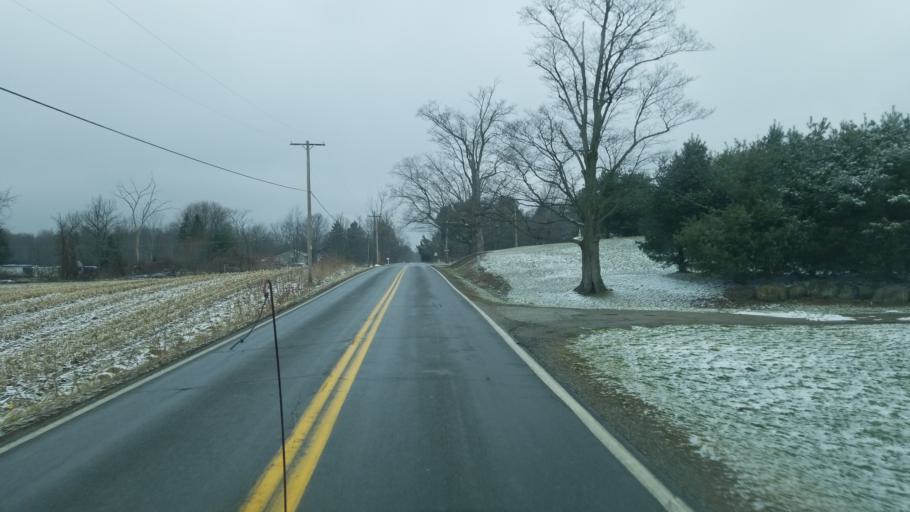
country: US
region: Ohio
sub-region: Portage County
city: Mantua
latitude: 41.2842
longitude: -81.2858
